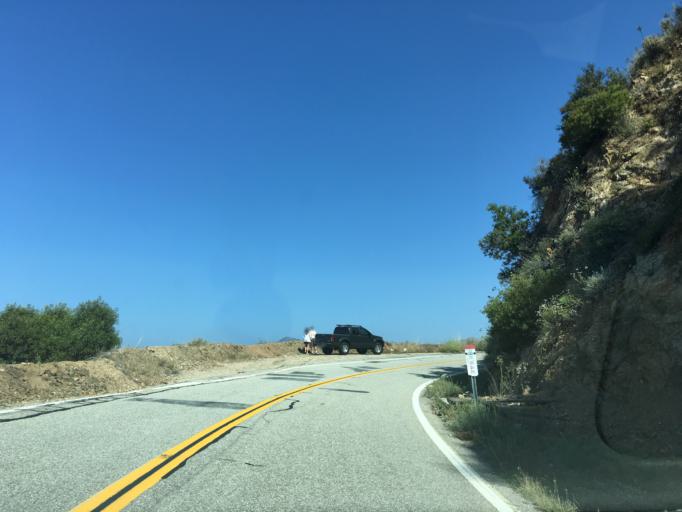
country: US
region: California
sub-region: Los Angeles County
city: Glendora
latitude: 34.1905
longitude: -117.8419
